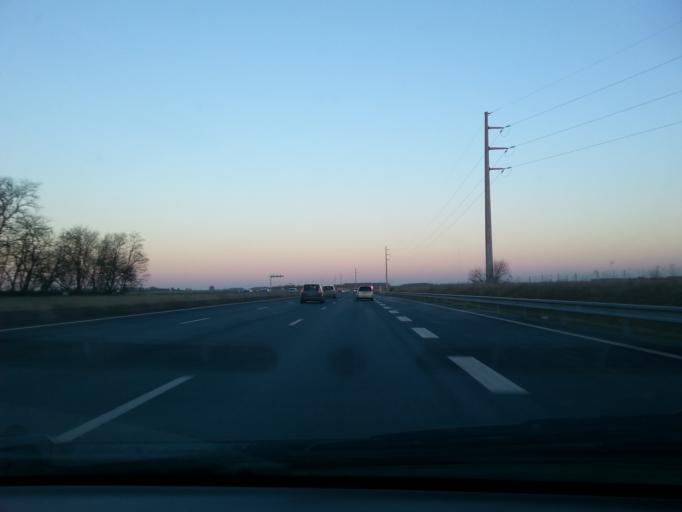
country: FR
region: Centre
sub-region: Departement d'Eure-et-Loir
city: Bailleau-le-Pin
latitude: 48.3240
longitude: 1.3661
